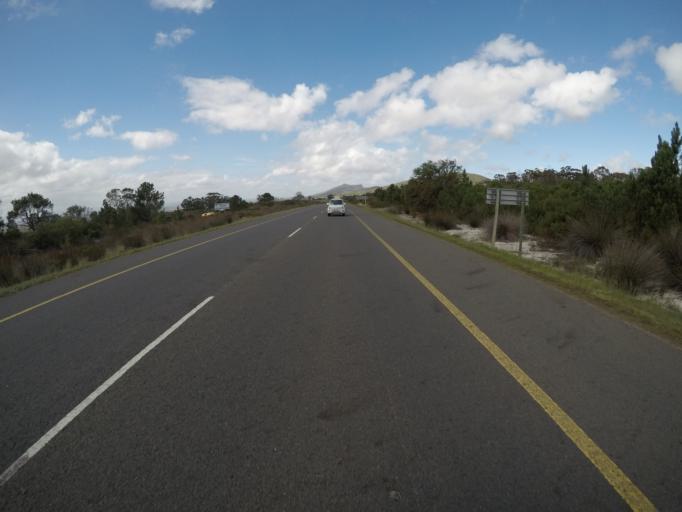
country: ZA
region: Western Cape
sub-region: Eden District Municipality
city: Riversdale
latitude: -34.2123
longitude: 21.5927
